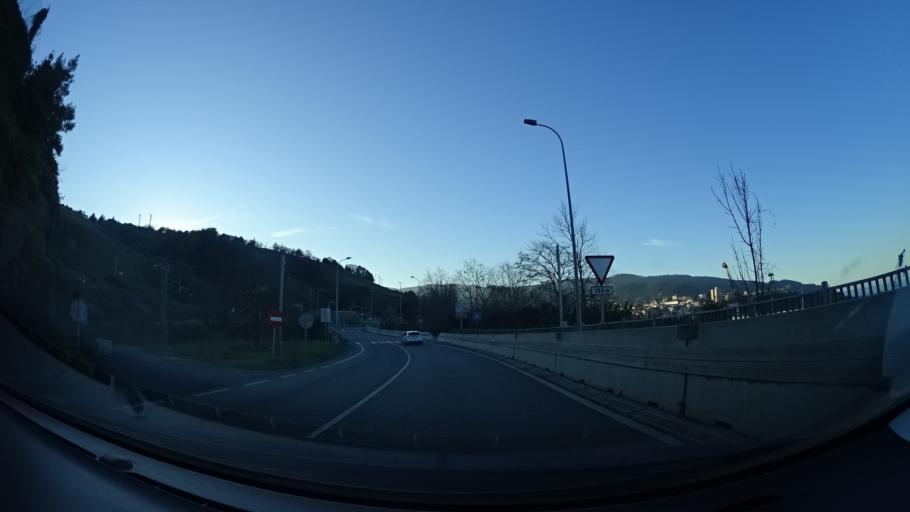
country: ES
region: Basque Country
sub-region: Bizkaia
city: Bermeo
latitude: 43.4172
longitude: -2.7124
